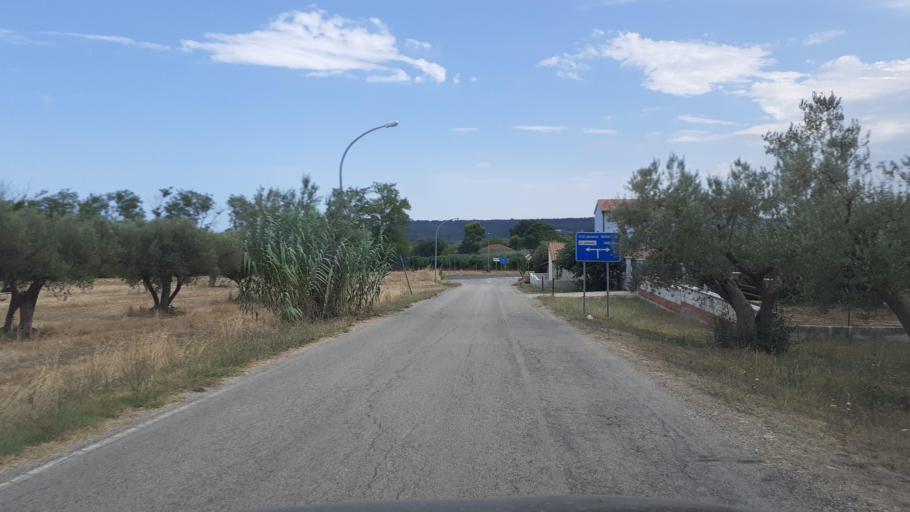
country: IT
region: Abruzzo
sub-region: Provincia di Chieti
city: Fossacesia
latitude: 42.2509
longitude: 14.5034
